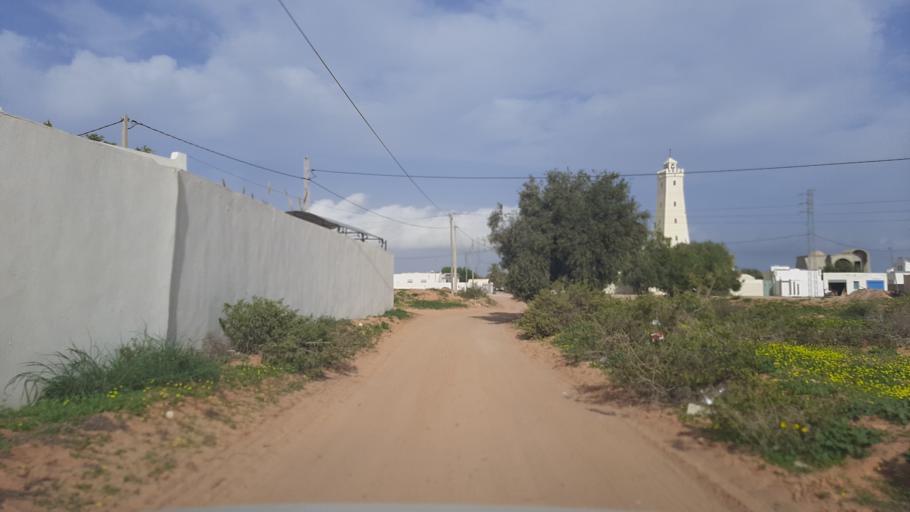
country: TN
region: Madanin
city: Midoun
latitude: 33.7974
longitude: 11.0292
